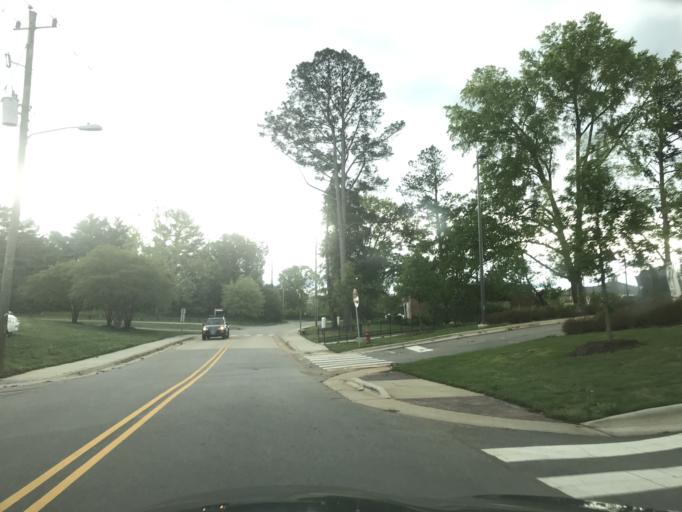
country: US
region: North Carolina
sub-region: Wake County
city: West Raleigh
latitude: 35.7812
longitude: -78.6808
